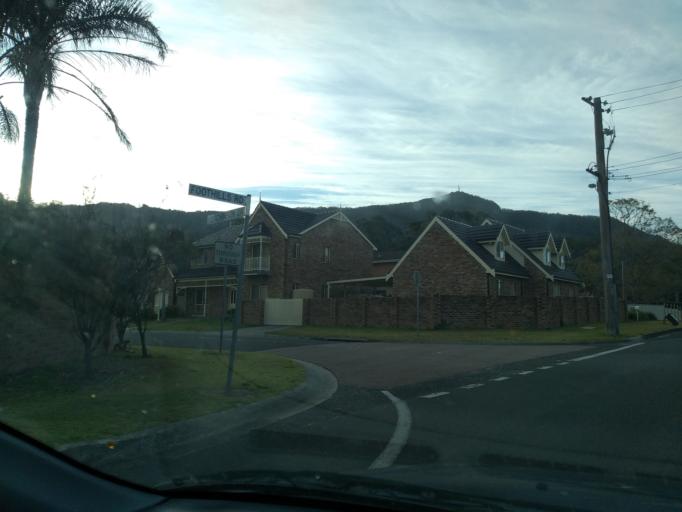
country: AU
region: New South Wales
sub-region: Wollongong
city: Mount Ousley
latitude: -34.3827
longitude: 150.8819
